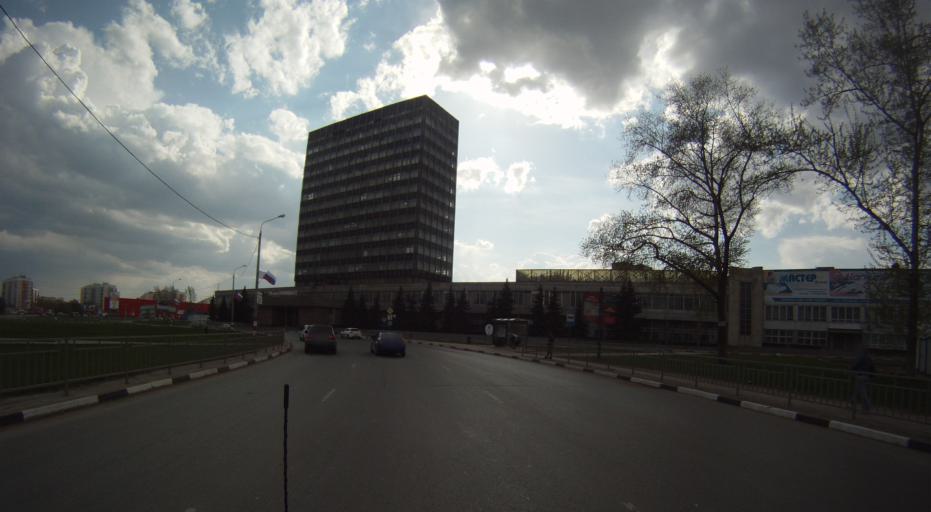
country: RU
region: Nizjnij Novgorod
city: Nizhniy Novgorod
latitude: 56.2995
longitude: 43.9445
